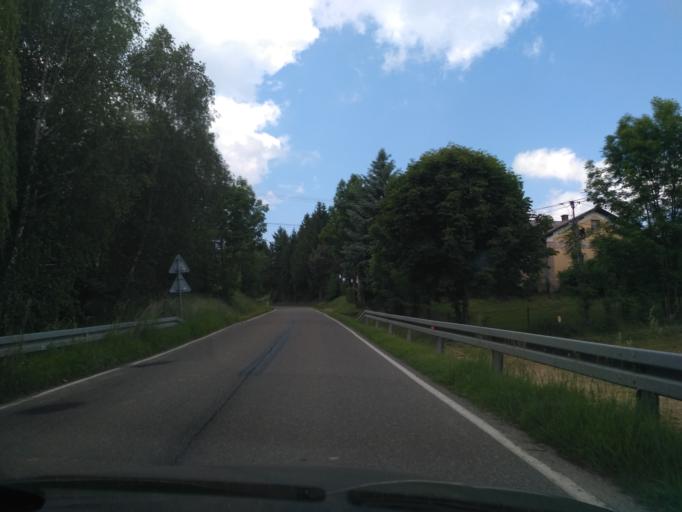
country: PL
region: Subcarpathian Voivodeship
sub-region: Powiat rzeszowski
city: Hyzne
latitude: 49.9558
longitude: 22.2013
